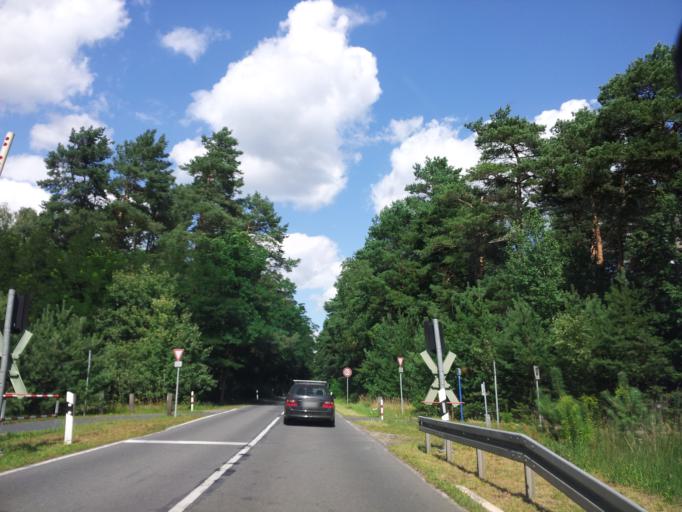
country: DE
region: Brandenburg
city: Niedergorsdorf
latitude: 51.9904
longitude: 13.0082
